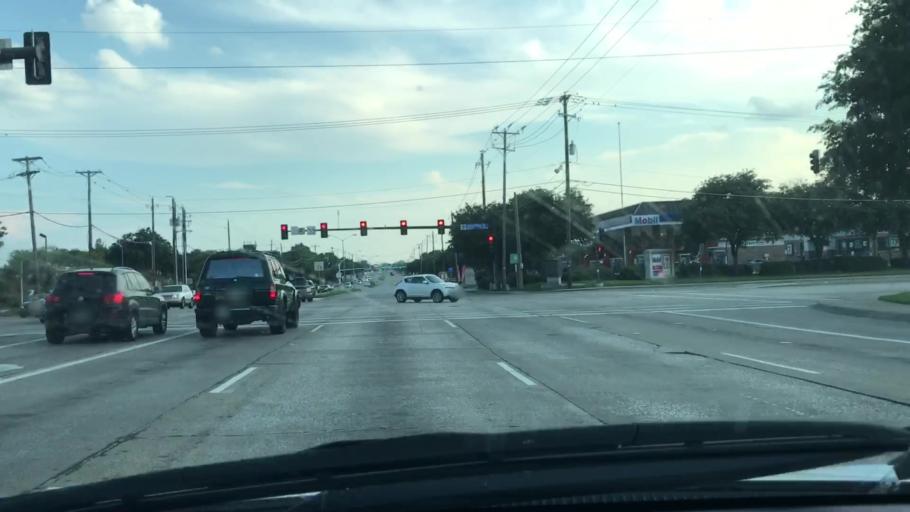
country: US
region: Texas
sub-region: Dallas County
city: Addison
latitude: 32.9404
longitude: -96.8390
